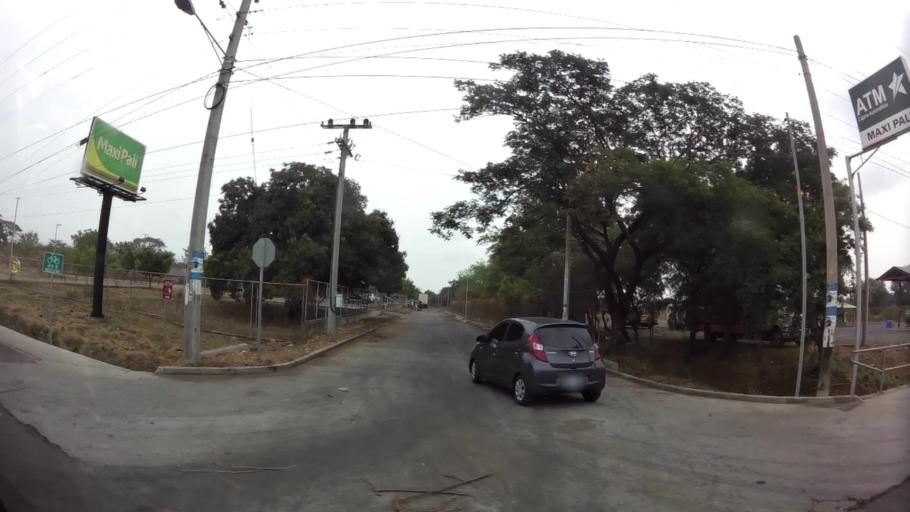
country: NI
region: Leon
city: Leon
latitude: 12.4567
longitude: -86.8666
